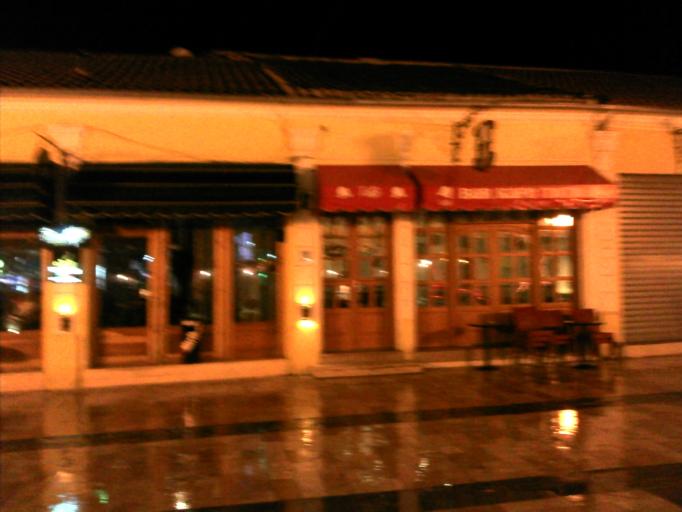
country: AL
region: Shkoder
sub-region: Rrethi i Shkodres
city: Shkoder
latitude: 42.0690
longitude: 19.5167
